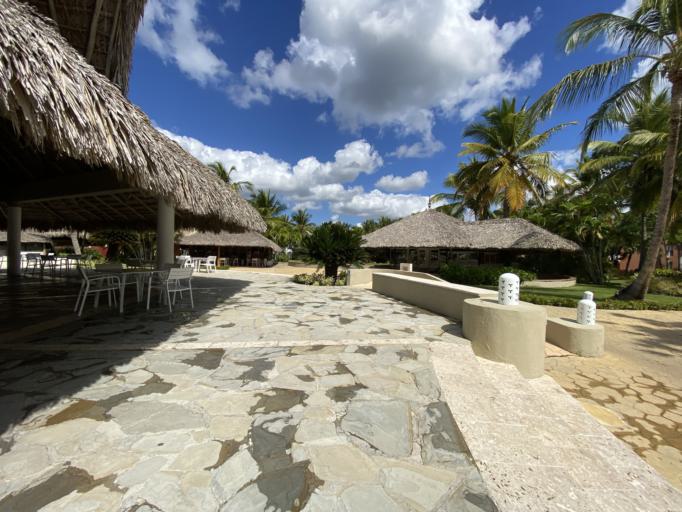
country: DO
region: La Altagracia
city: San Rafael del Yuma
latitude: 18.3439
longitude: -68.8224
